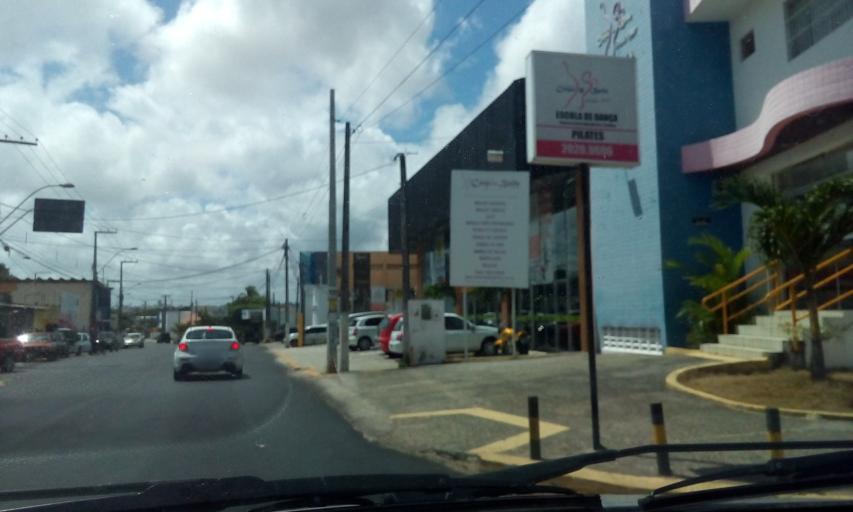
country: BR
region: Rio Grande do Norte
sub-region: Natal
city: Natal
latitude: -5.8602
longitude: -35.2057
